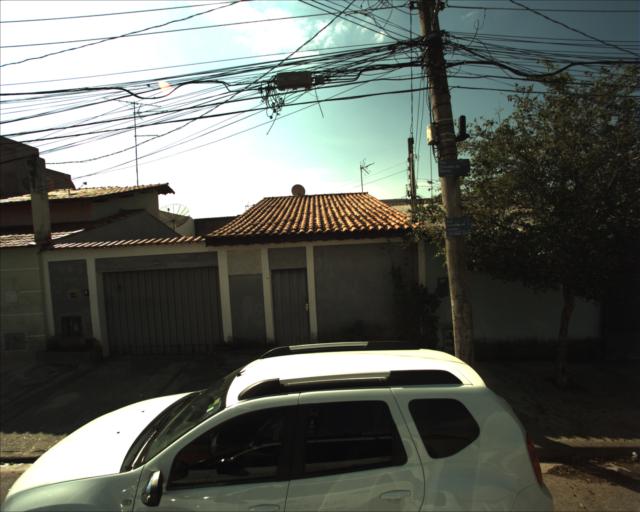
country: BR
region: Sao Paulo
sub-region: Sorocaba
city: Sorocaba
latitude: -23.4991
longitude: -47.5153
